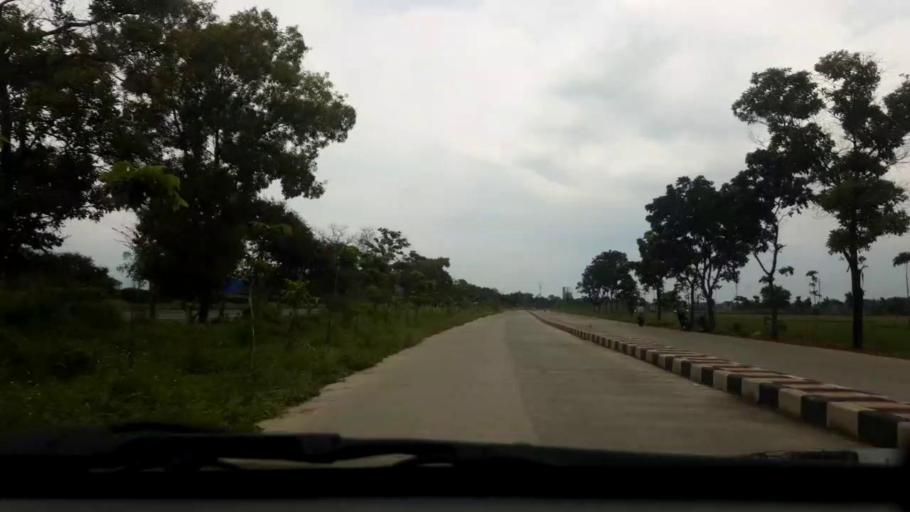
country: ID
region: West Java
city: Cileunyi
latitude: -6.9634
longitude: 107.7120
